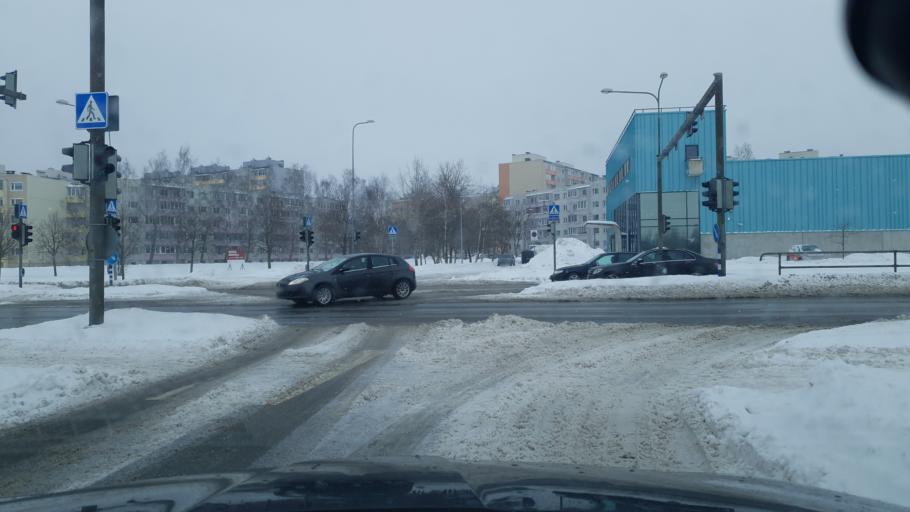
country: EE
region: Harju
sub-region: Tallinna linn
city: Kose
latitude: 59.4385
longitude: 24.8700
